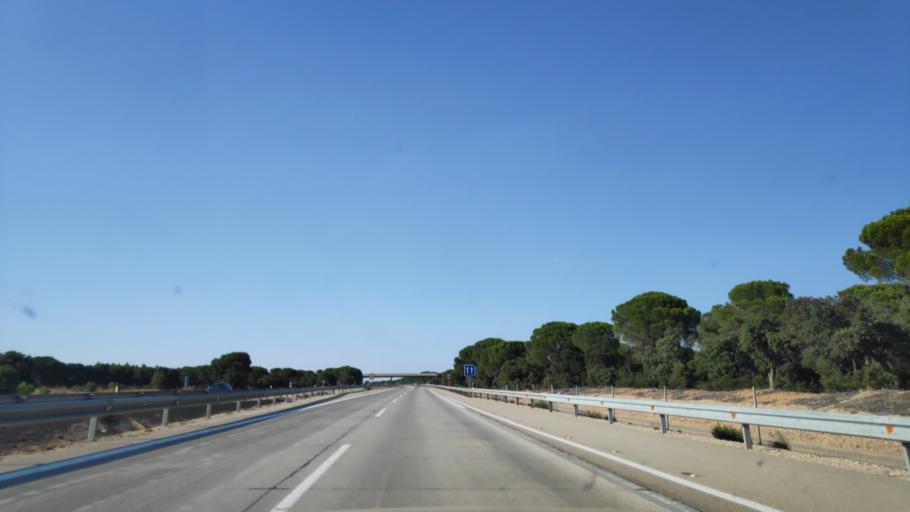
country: ES
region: Castille-La Mancha
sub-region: Provincia de Cuenca
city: Pozoamargo
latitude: 39.3275
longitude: -2.2017
